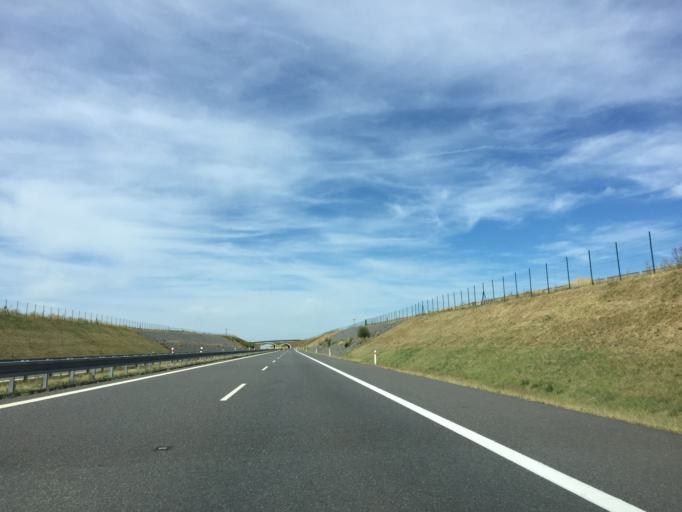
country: CZ
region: Jihocesky
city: Sobeslav
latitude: 49.3005
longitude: 14.7371
